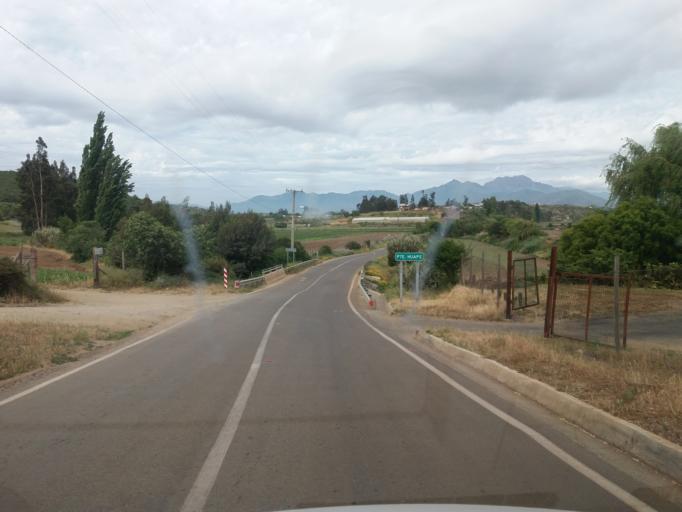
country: CL
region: Valparaiso
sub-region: Provincia de Quillota
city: Quillota
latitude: -32.9164
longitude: -71.3563
